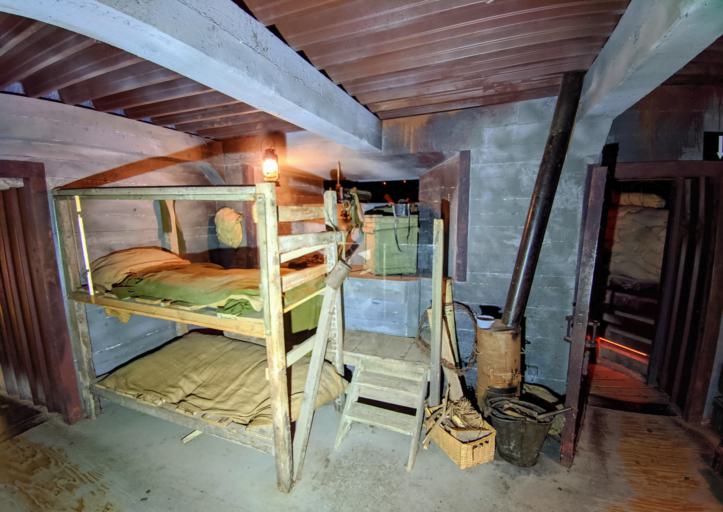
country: BE
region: Wallonia
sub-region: Province de Namur
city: Dinant
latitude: 50.2618
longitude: 4.9134
